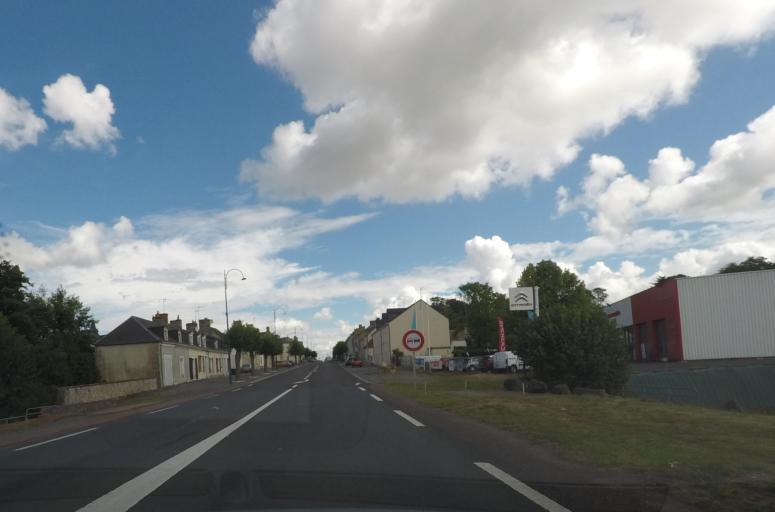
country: FR
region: Pays de la Loire
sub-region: Departement de la Sarthe
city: Cerans-Foulletourte
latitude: 47.8244
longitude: 0.0729
